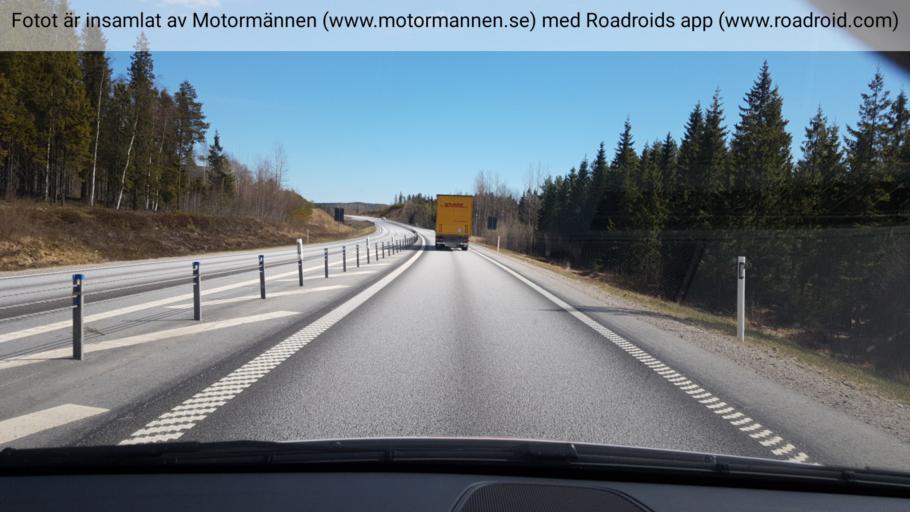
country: SE
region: Vaesterbotten
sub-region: Vannas Kommun
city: Vannasby
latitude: 63.9020
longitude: 19.8976
